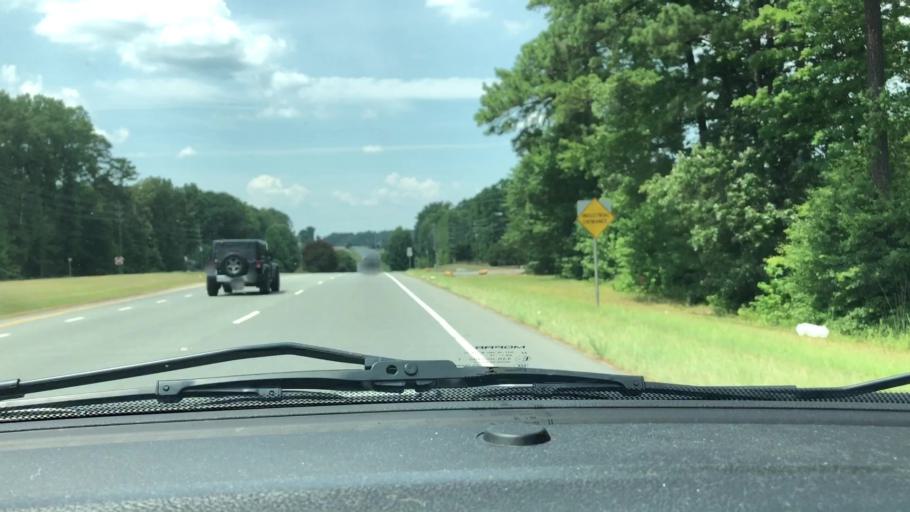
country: US
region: North Carolina
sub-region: Lee County
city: Sanford
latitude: 35.5068
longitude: -79.2088
